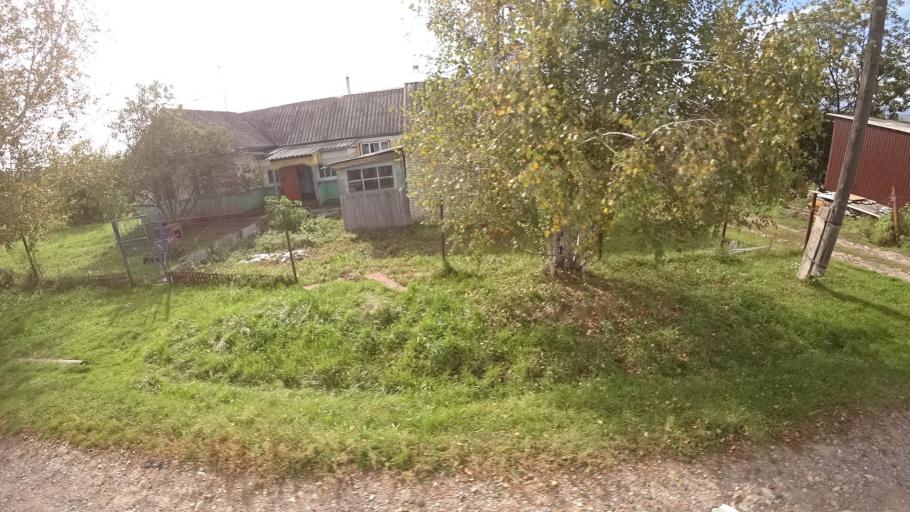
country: RU
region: Primorskiy
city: Dostoyevka
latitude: 44.3261
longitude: 133.4868
